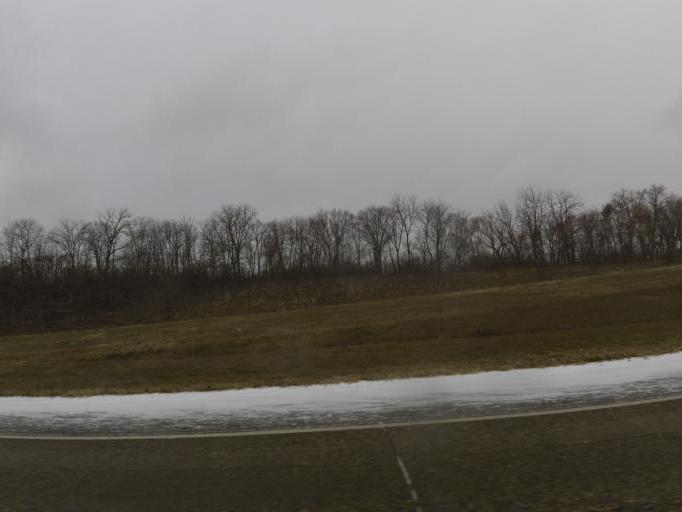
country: US
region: Minnesota
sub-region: Dakota County
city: Eagan
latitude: 44.8029
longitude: -93.2219
